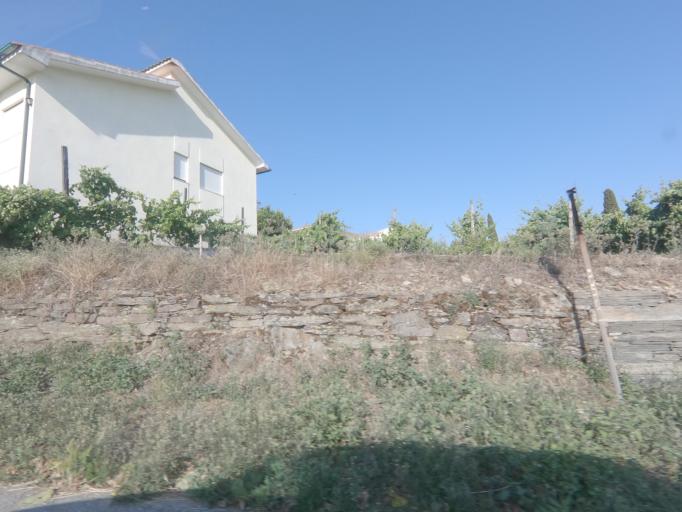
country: PT
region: Vila Real
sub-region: Sabrosa
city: Vilela
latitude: 41.1813
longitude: -7.6059
